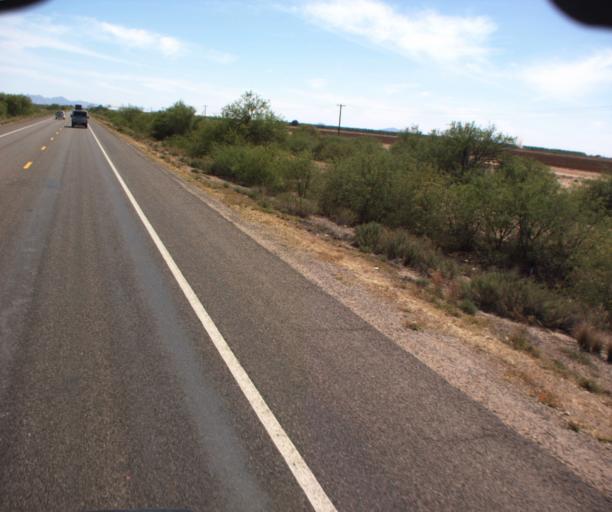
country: US
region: Arizona
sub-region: Pinal County
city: Eloy
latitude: 32.7481
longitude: -111.5159
